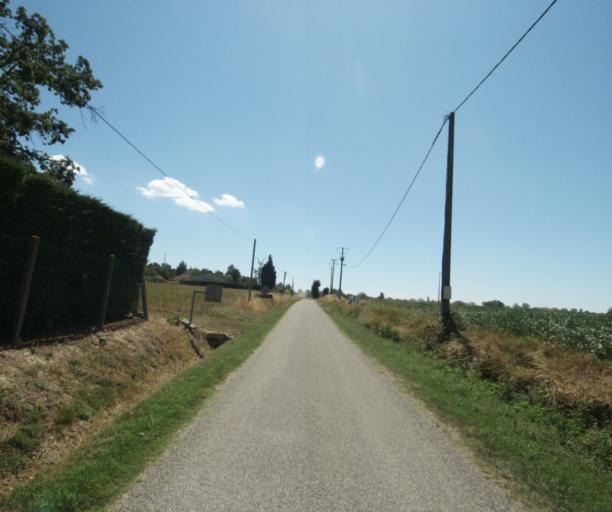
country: FR
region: Midi-Pyrenees
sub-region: Departement de la Haute-Garonne
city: Saint-Felix-Lauragais
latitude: 43.4550
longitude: 1.9462
